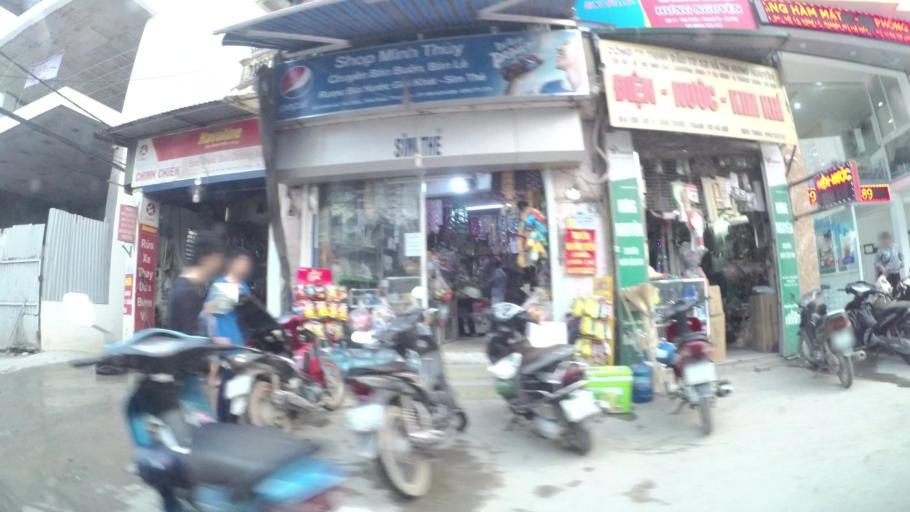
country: VN
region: Ha Noi
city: Thanh Xuan
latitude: 20.9798
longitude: 105.8063
